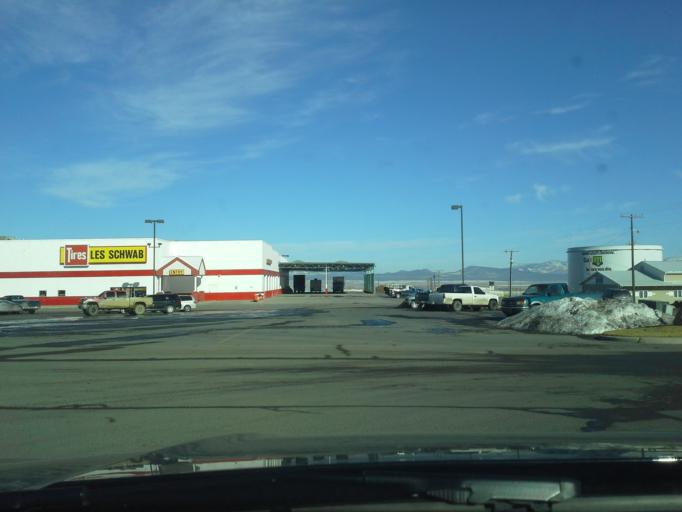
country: US
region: Montana
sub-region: Lewis and Clark County
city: Helena
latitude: 46.5923
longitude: -111.9865
